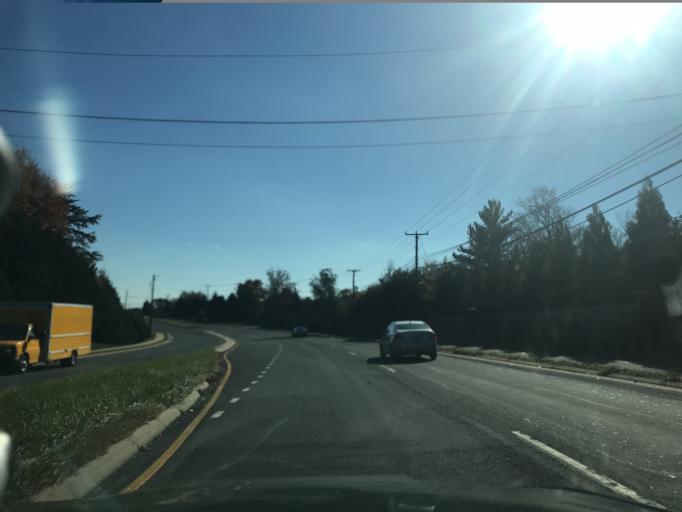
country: US
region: Virginia
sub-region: Fairfax County
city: Greenbriar
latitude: 38.8941
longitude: -77.3806
